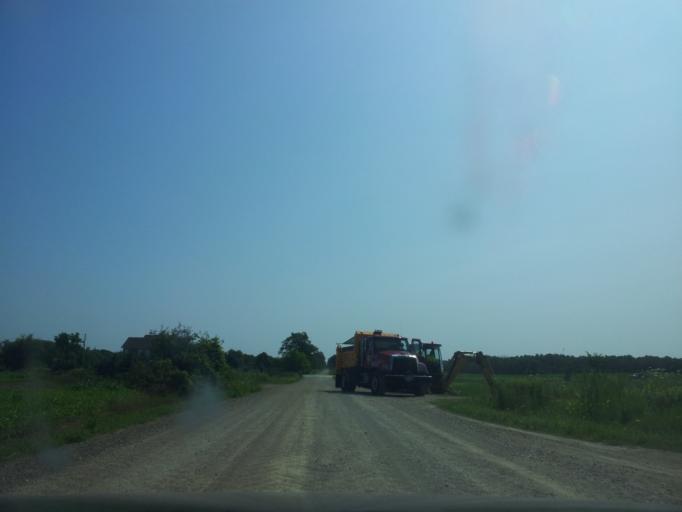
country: CA
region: Ontario
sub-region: Oxford County
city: Woodstock
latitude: 42.9518
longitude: -80.6357
